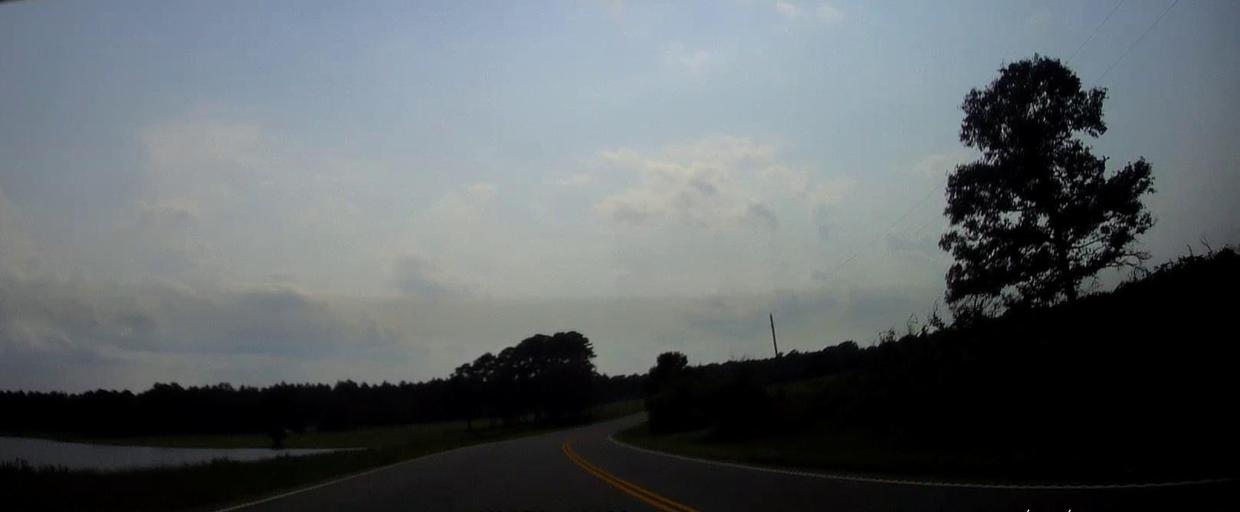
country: US
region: Georgia
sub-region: Twiggs County
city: Jeffersonville
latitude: 32.5764
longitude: -83.3989
